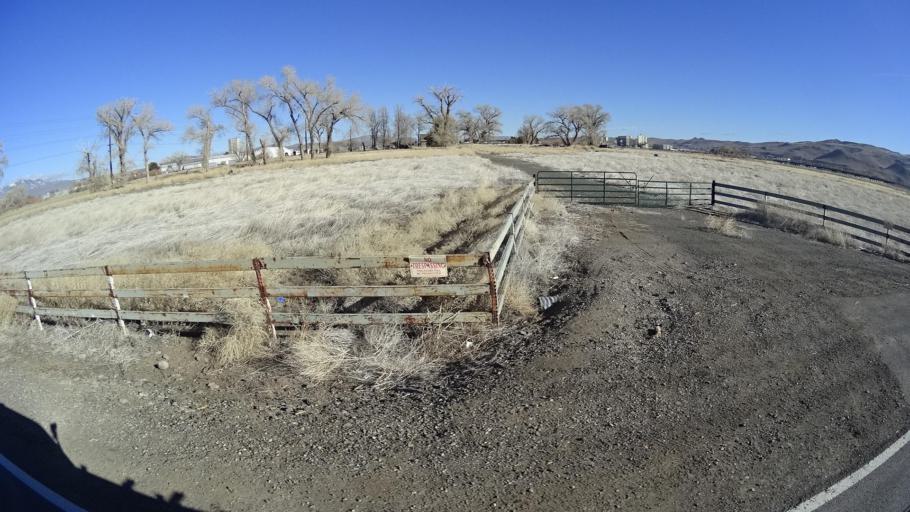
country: US
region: Nevada
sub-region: Washoe County
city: Sparks
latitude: 39.5125
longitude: -119.7195
